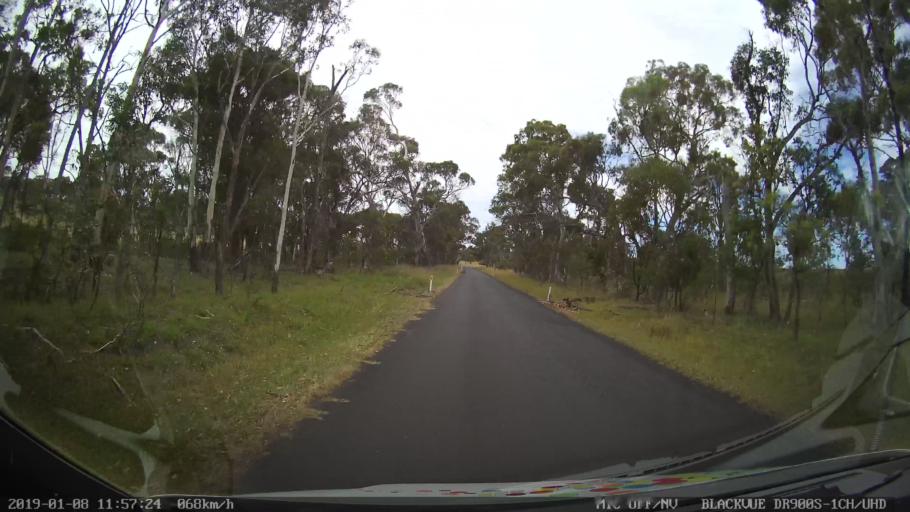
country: AU
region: New South Wales
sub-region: Armidale Dumaresq
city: Armidale
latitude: -30.4497
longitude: 151.5669
